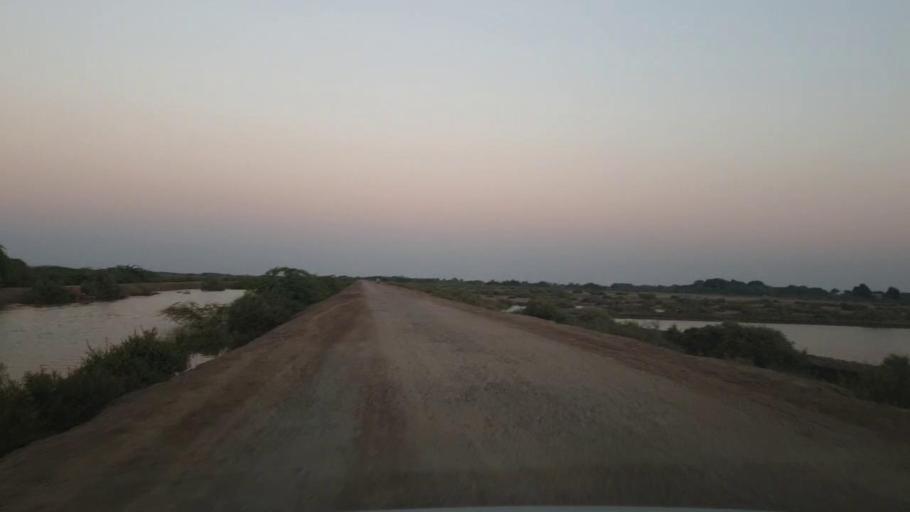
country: PK
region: Sindh
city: Mirpur Sakro
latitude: 24.3865
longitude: 67.5792
